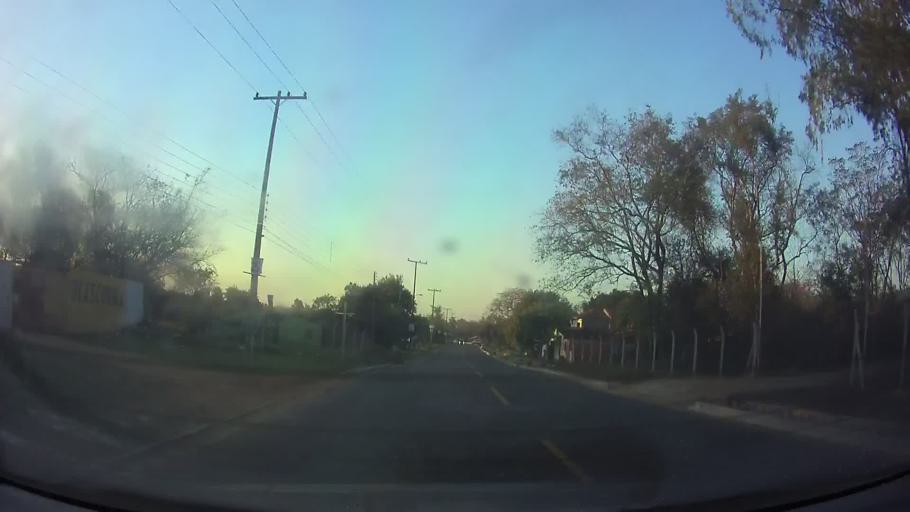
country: PY
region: Central
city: Limpio
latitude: -25.2381
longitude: -57.4909
